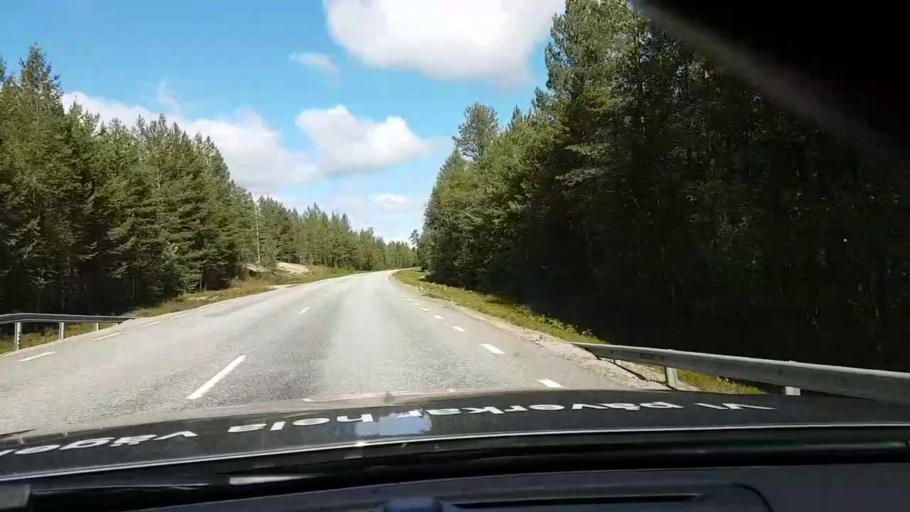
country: SE
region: Vaesternorrland
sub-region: OErnskoeldsviks Kommun
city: Bredbyn
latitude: 63.6236
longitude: 17.9073
